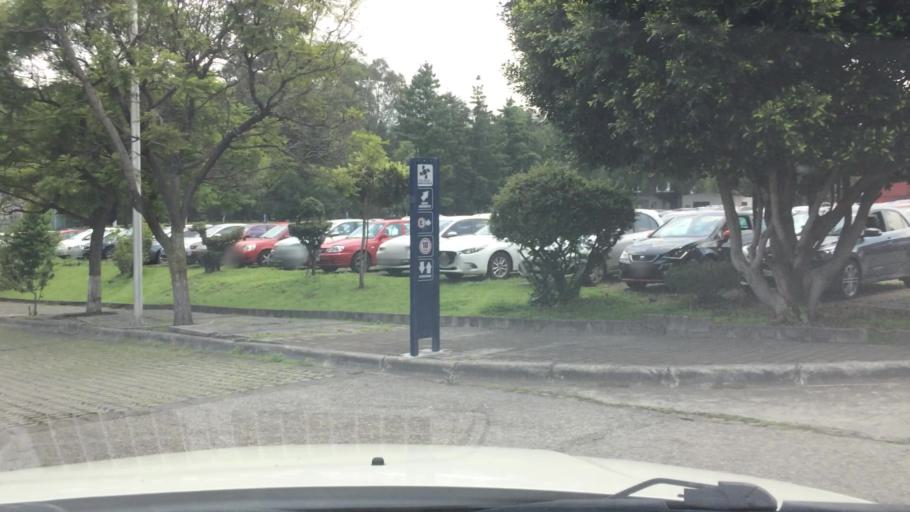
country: MX
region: Mexico City
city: Tlalpan
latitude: 19.2995
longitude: -99.1842
